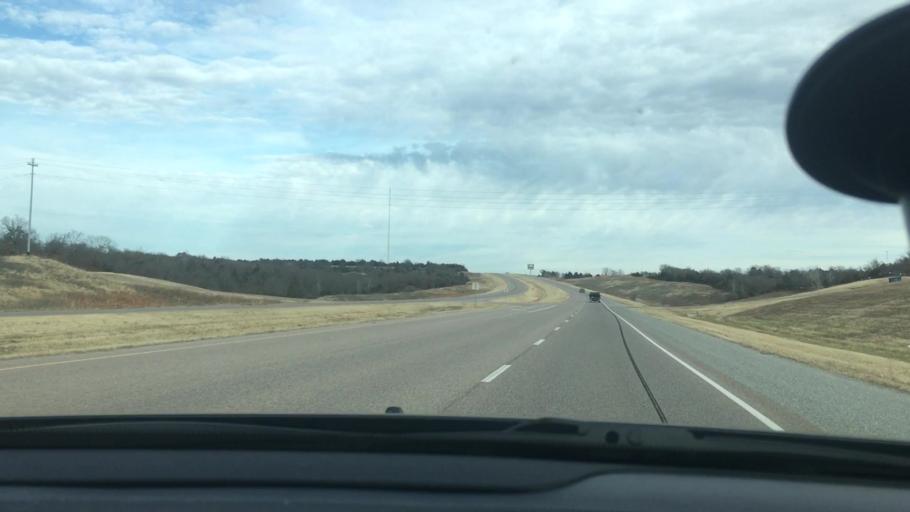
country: US
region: Oklahoma
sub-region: Pontotoc County
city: Byng
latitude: 34.8819
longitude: -96.6761
